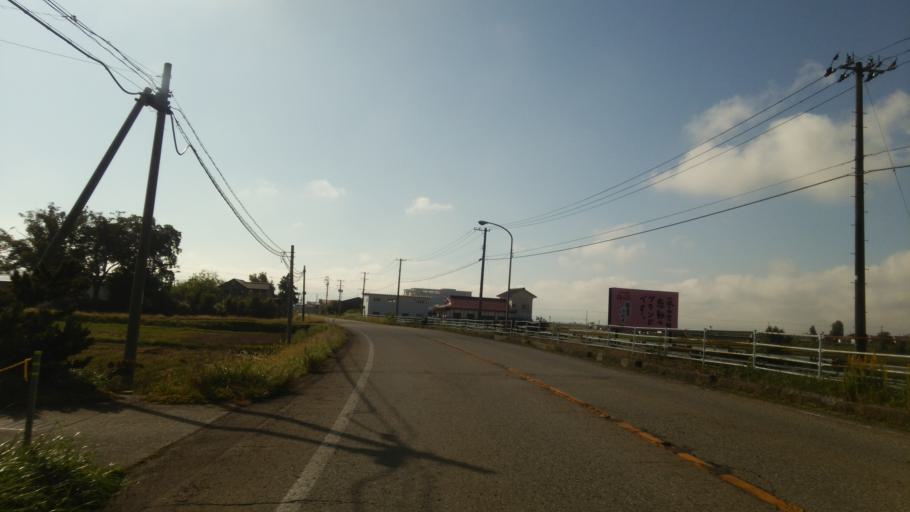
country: JP
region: Fukushima
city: Kitakata
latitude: 37.5588
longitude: 139.9068
